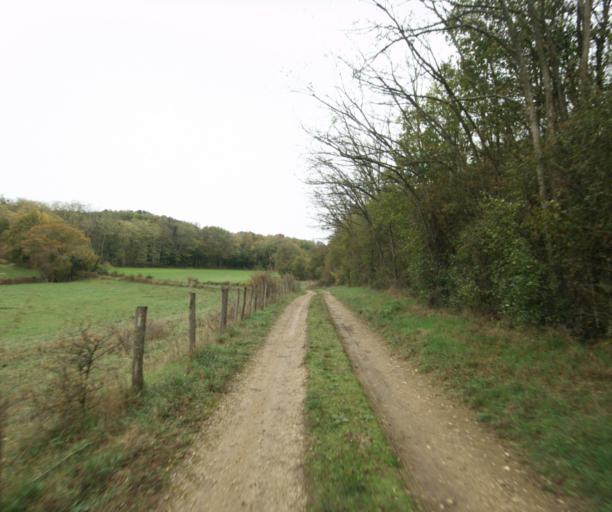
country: FR
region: Bourgogne
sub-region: Departement de Saone-et-Loire
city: Tournus
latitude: 46.4886
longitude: 4.8586
